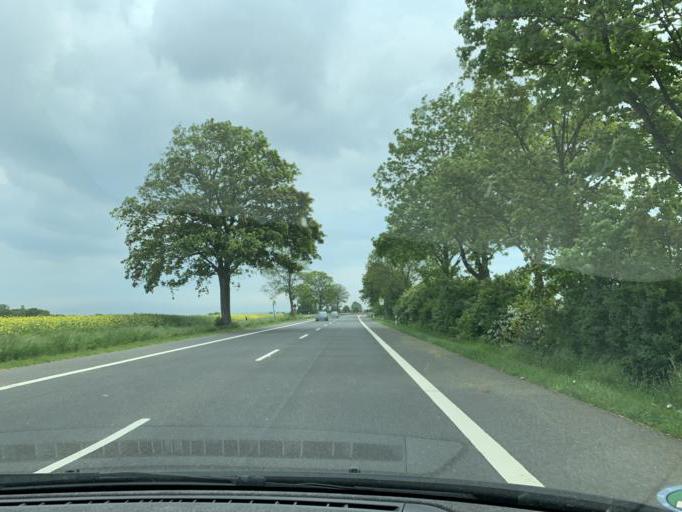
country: DE
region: North Rhine-Westphalia
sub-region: Regierungsbezirk Koln
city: Norvenich
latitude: 50.7806
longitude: 6.6342
